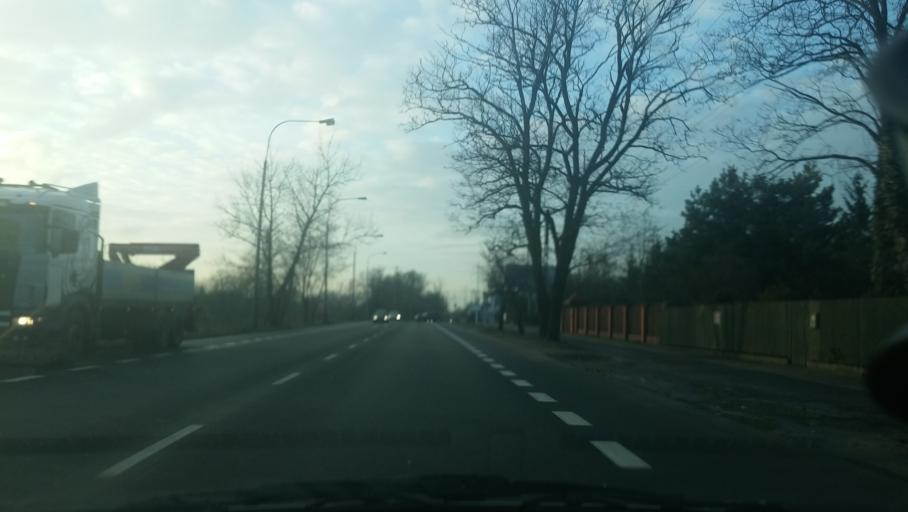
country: PL
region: Masovian Voivodeship
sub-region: Warszawa
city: Wawer
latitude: 52.2163
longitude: 21.1574
